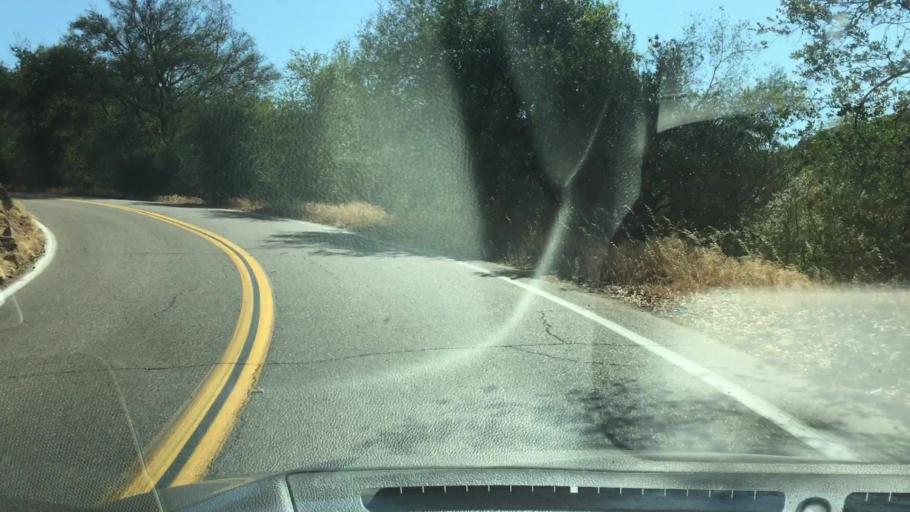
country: US
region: California
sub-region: San Diego County
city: Harbison Canyon
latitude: 32.7501
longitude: -116.7882
